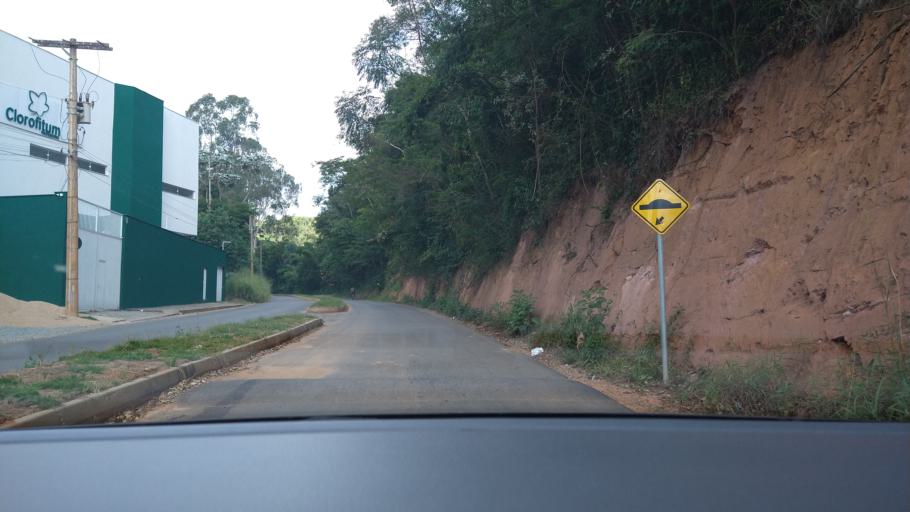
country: BR
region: Minas Gerais
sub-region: Vicosa
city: Vicosa
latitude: -20.7795
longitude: -42.8523
